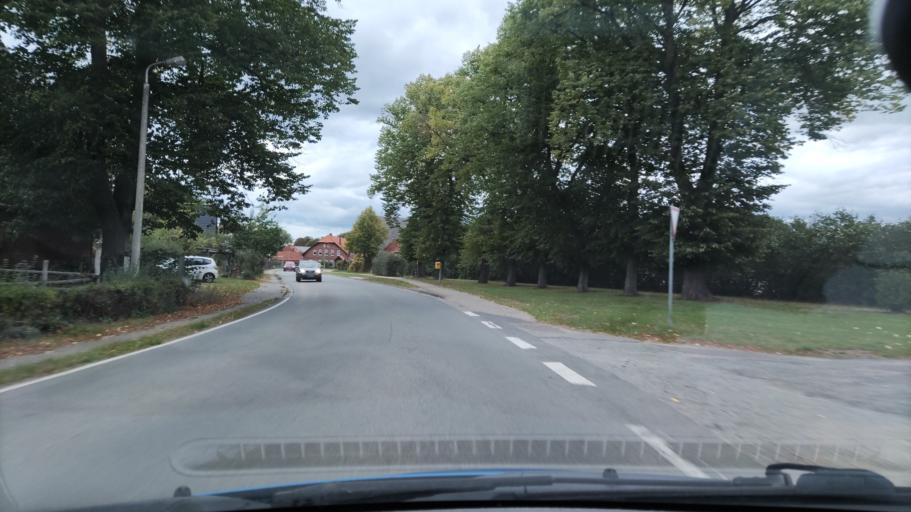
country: DE
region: Lower Saxony
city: Neu Darchau
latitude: 53.3165
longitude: 10.9576
